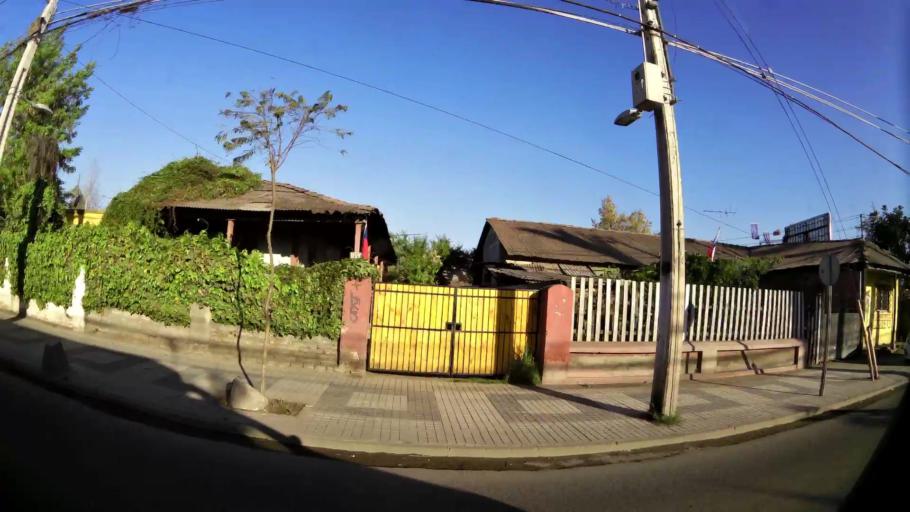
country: CL
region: Santiago Metropolitan
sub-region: Provincia de Talagante
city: Penaflor
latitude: -33.6093
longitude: -70.8569
